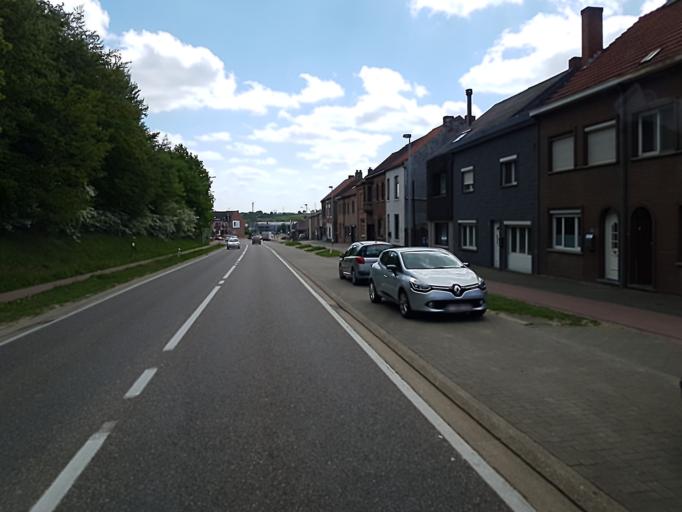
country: BE
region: Flanders
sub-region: Provincie Vlaams-Brabant
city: Diest
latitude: 50.9814
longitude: 5.0410
